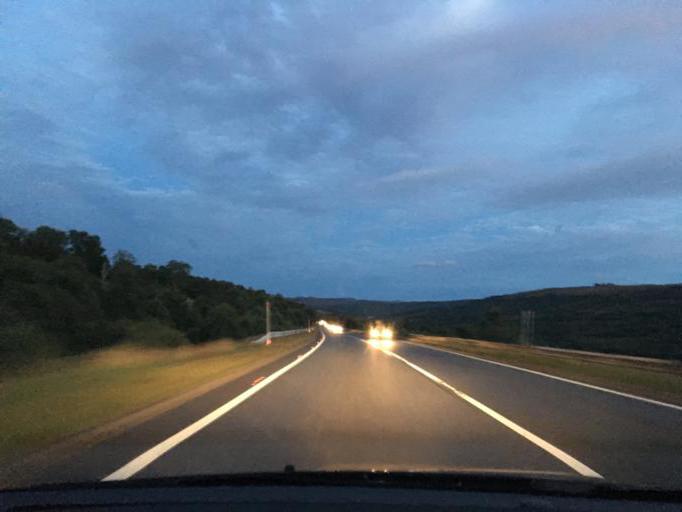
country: GB
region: Scotland
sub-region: Perth and Kinross
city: Aberfeldy
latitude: 56.7844
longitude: -4.0049
